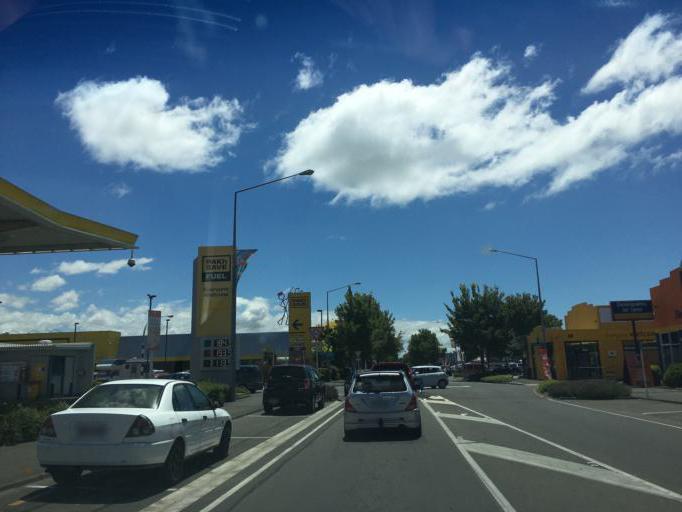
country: NZ
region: Hawke's Bay
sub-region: Hastings District
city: Hastings
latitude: -39.6373
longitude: 176.8383
